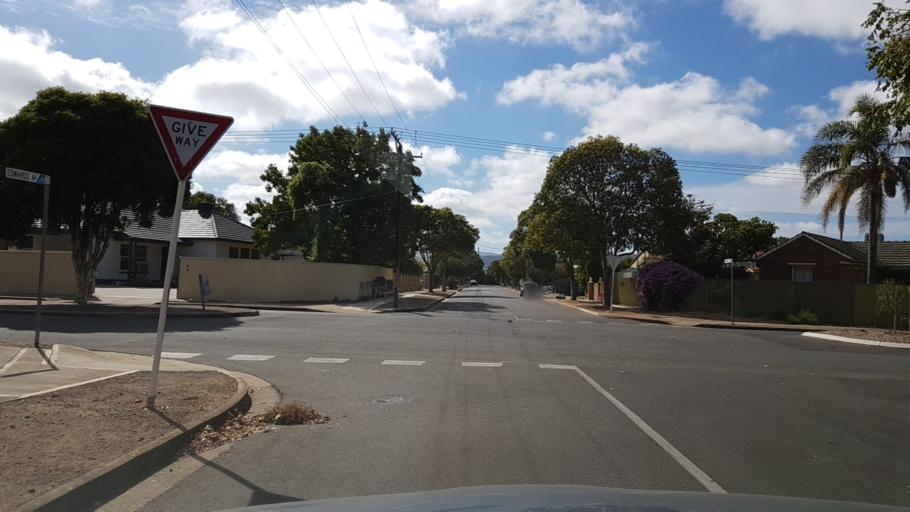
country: AU
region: South Australia
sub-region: Marion
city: Plympton Park
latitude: -34.9945
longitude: 138.5511
